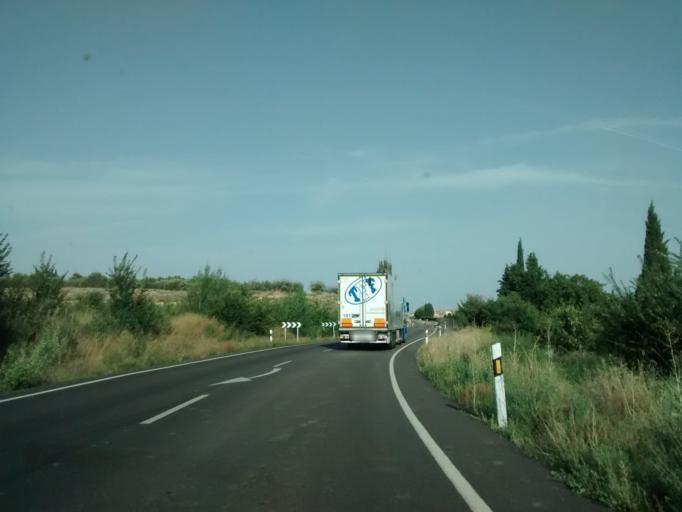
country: ES
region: Aragon
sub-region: Provincia de Zaragoza
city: Malejan
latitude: 41.8298
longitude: -1.5591
